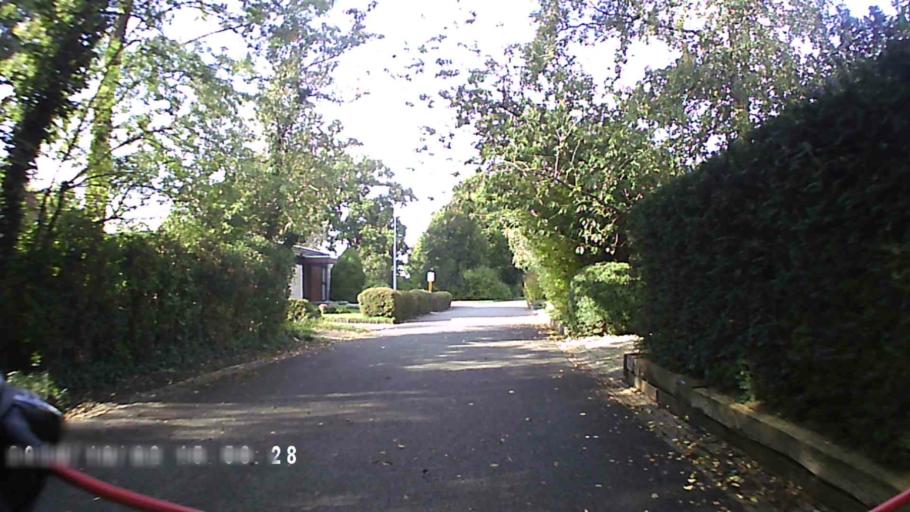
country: NL
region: Groningen
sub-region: Gemeente Zuidhorn
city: Zuidhorn
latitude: 53.2465
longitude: 6.4044
